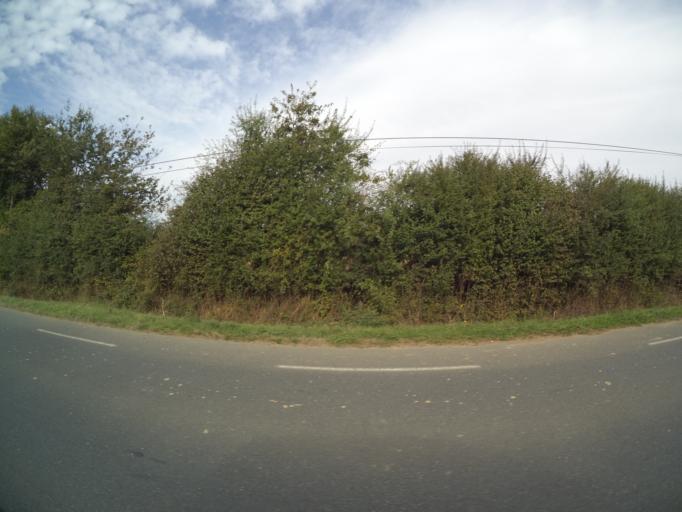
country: FR
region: Pays de la Loire
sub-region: Departement de Maine-et-Loire
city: Jallais
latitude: 47.2099
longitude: -0.8121
